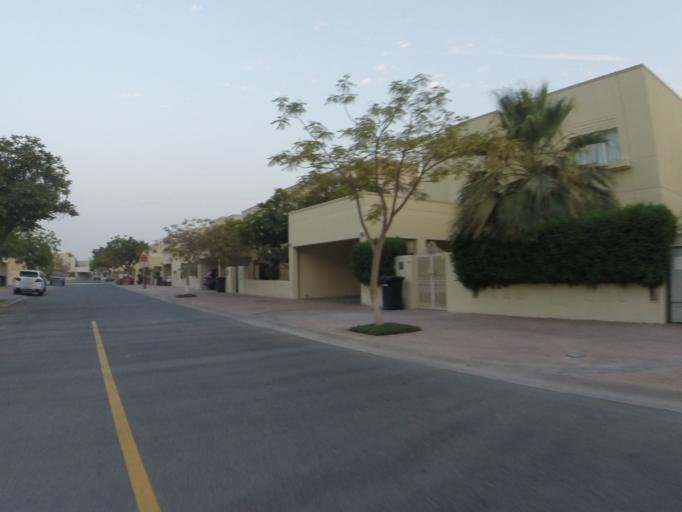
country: AE
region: Dubai
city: Dubai
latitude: 25.0697
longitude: 55.1486
